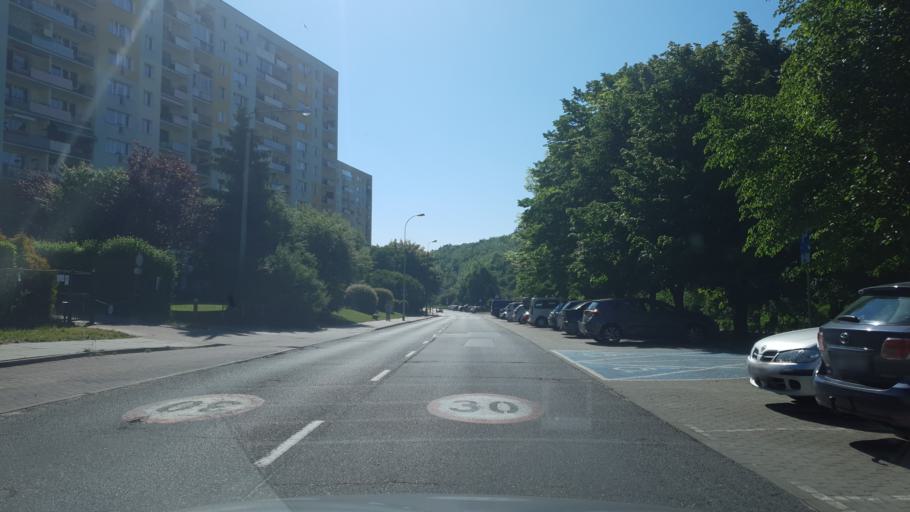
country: PL
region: Pomeranian Voivodeship
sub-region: Sopot
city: Sopot
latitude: 54.4571
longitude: 18.5378
